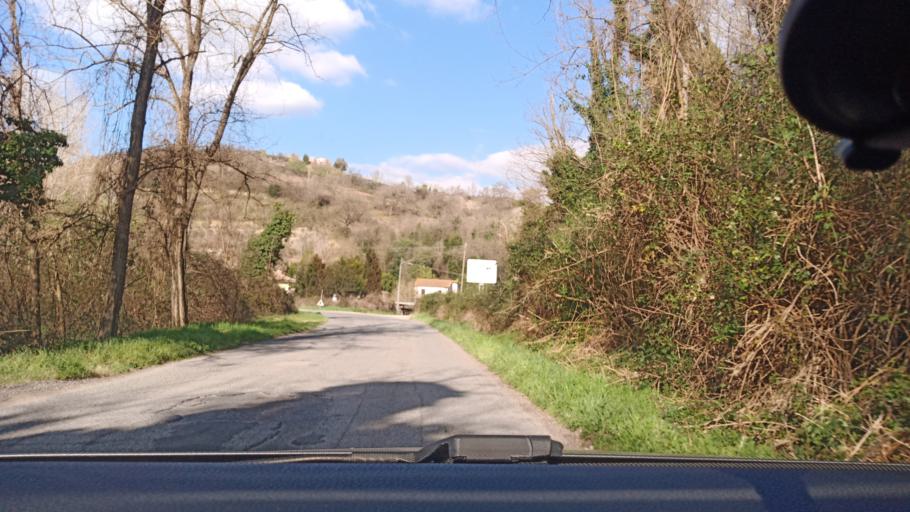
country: IT
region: Latium
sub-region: Citta metropolitana di Roma Capitale
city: Torrita Tiberina
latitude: 42.2375
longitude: 12.6336
